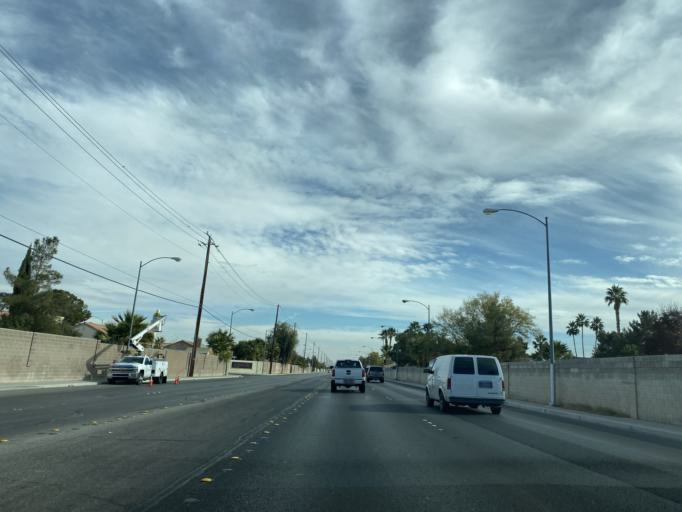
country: US
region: Nevada
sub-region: Clark County
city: Las Vegas
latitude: 36.2467
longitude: -115.2049
